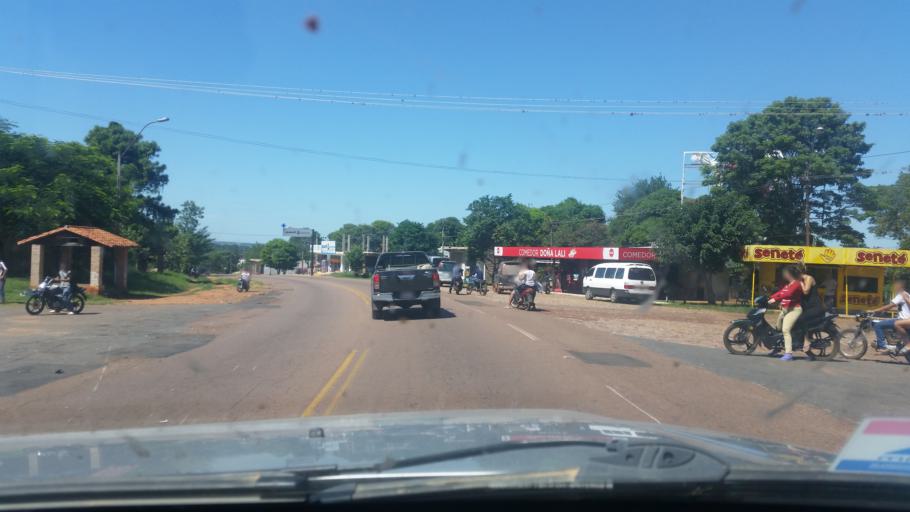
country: PY
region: Paraguari
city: Quiindy
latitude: -25.8818
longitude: -57.2900
